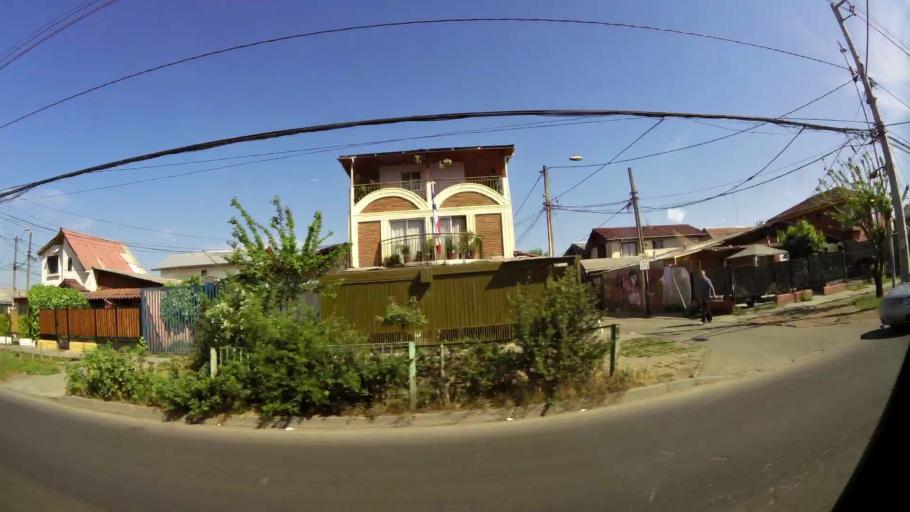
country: CL
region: Santiago Metropolitan
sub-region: Provincia de Santiago
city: Lo Prado
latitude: -33.4759
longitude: -70.7490
